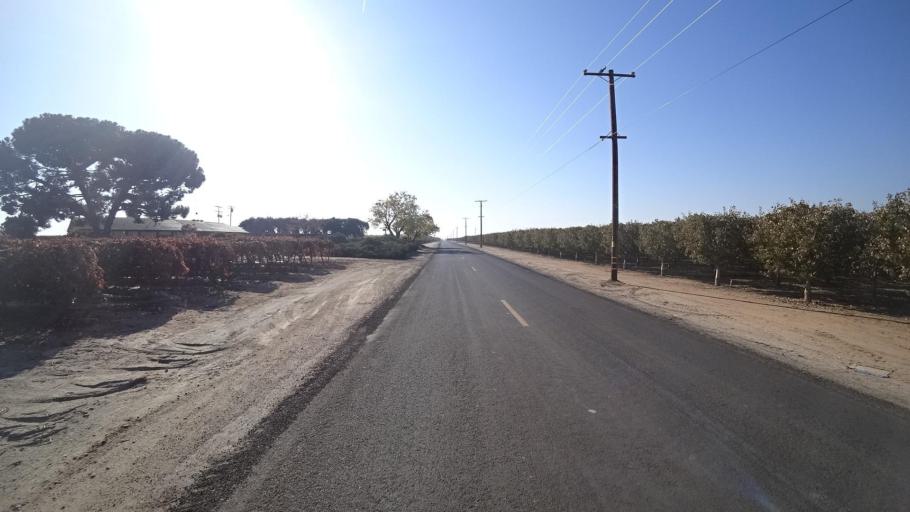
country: US
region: California
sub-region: Tulare County
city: Richgrove
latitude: 35.7423
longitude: -119.1342
